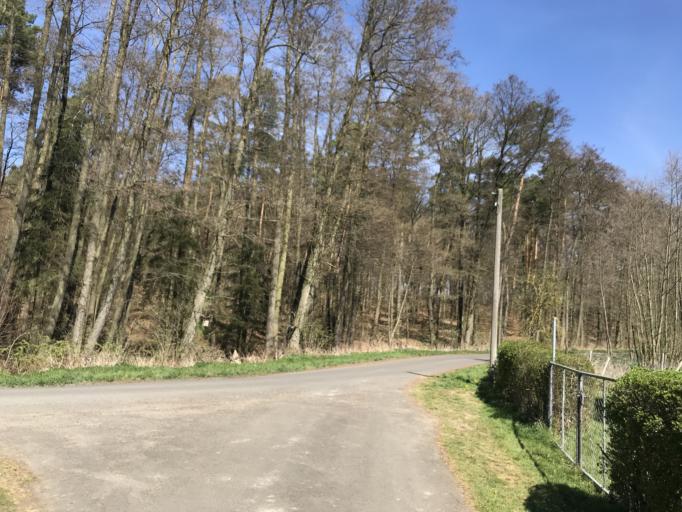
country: DE
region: Hesse
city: Staufenberg
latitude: 50.6446
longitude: 8.7451
